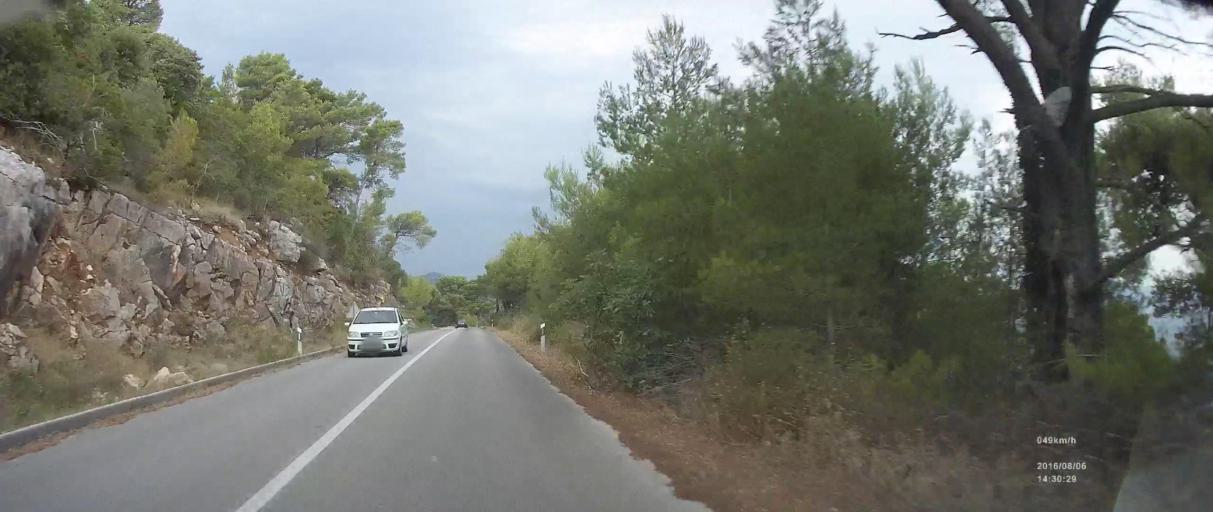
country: HR
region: Dubrovacko-Neretvanska
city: Ston
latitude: 42.7109
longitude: 17.7279
